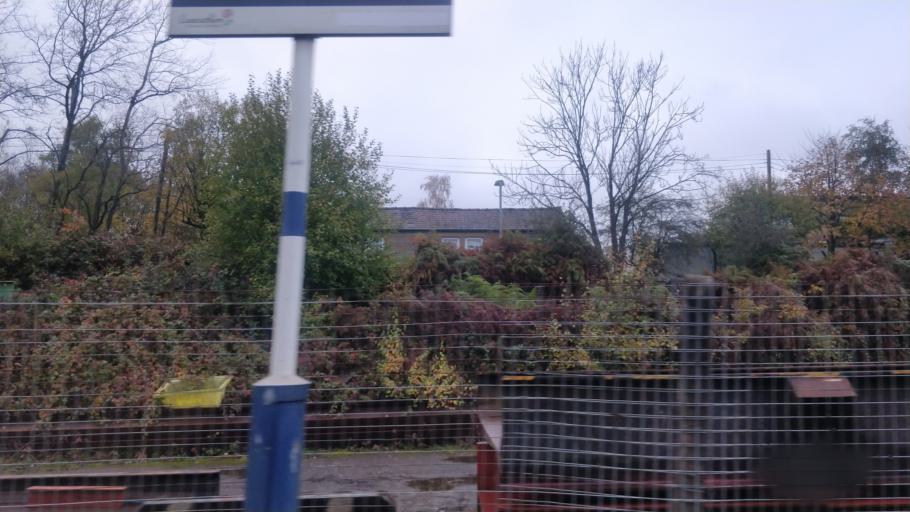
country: GB
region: England
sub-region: Lancashire
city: Appley Bridge
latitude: 53.5789
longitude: -2.7202
